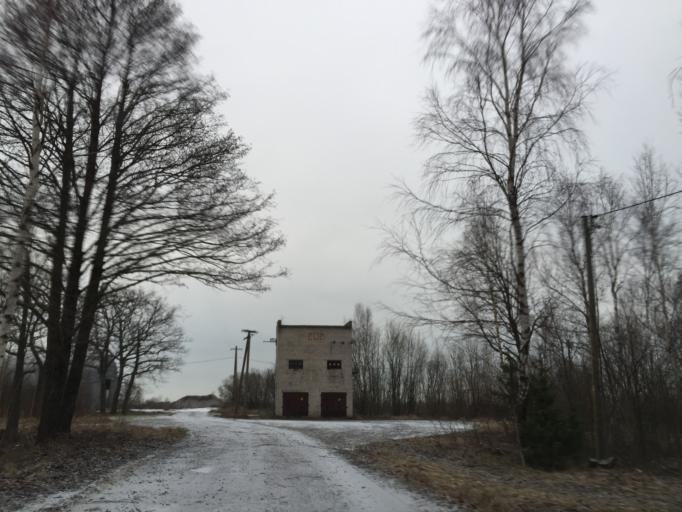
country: EE
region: Saare
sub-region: Orissaare vald
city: Orissaare
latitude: 58.6815
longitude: 23.1943
